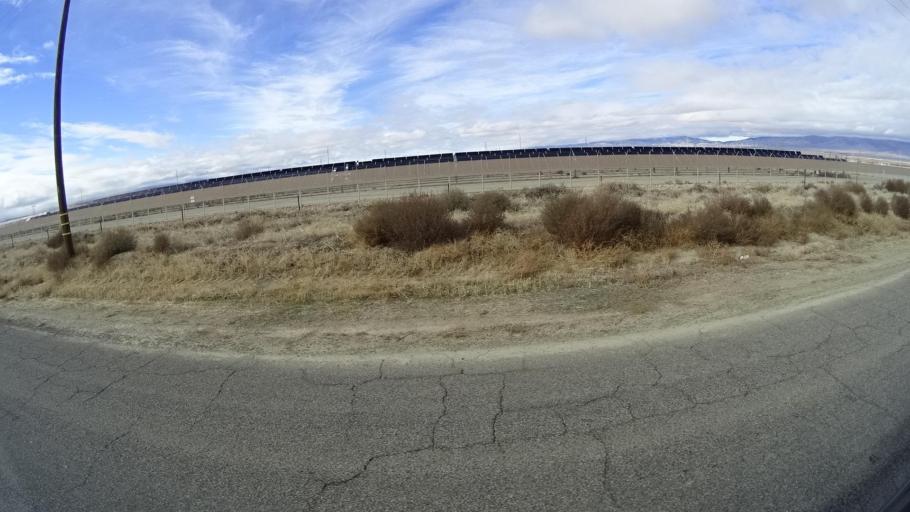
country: US
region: California
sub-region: Kern County
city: Rosamond
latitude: 34.8481
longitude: -118.3089
